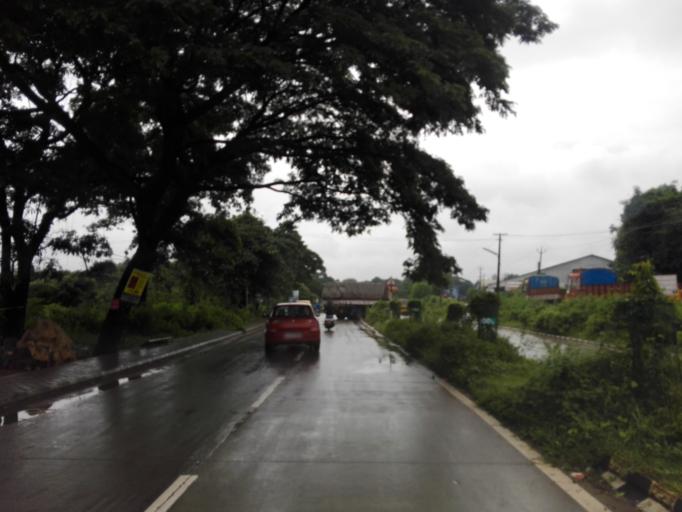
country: IN
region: Kerala
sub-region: Ernakulam
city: Elur
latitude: 10.0507
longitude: 76.3355
